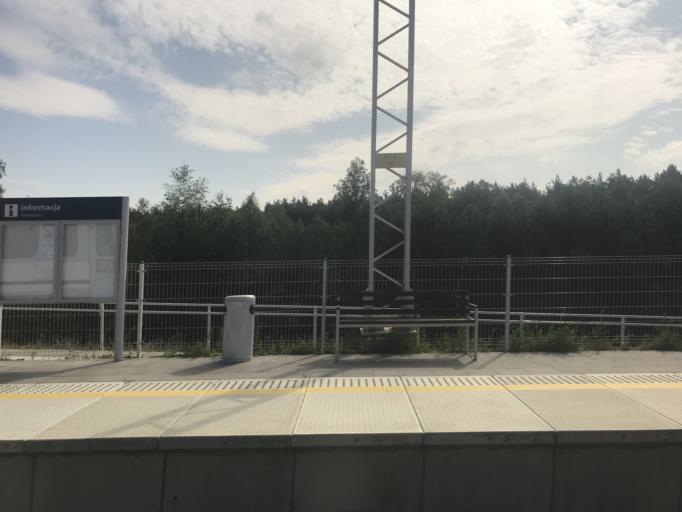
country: PL
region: Kujawsko-Pomorskie
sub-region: Bydgoszcz
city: Bydgoszcz
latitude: 53.1519
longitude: 18.0055
